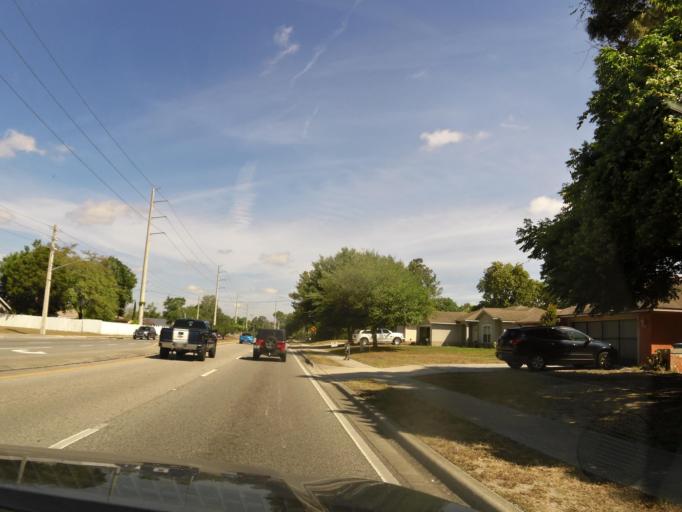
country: US
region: Florida
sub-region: Volusia County
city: Deltona
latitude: 28.9149
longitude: -81.1819
